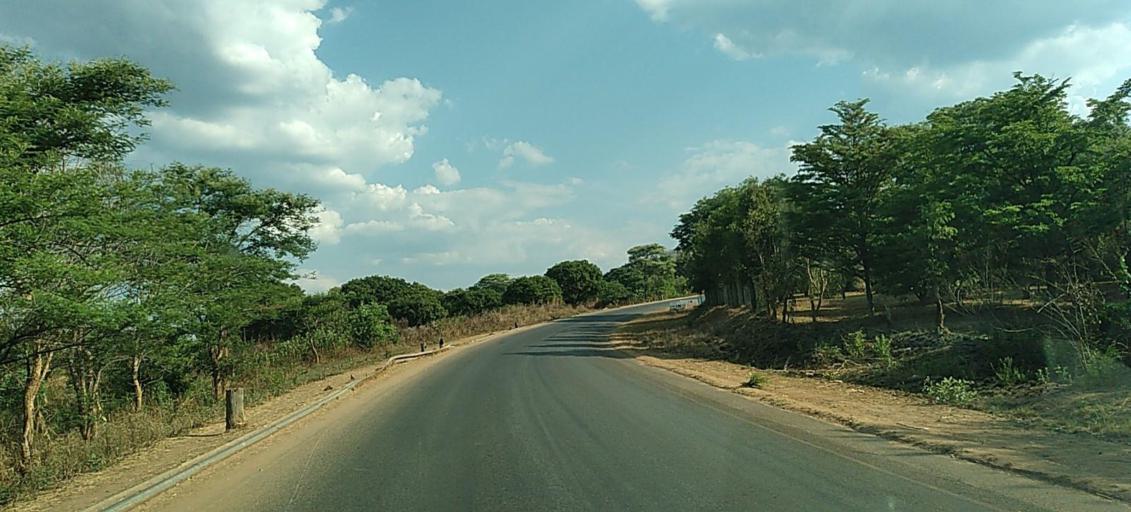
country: ZM
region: Copperbelt
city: Luanshya
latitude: -13.3474
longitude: 28.4205
